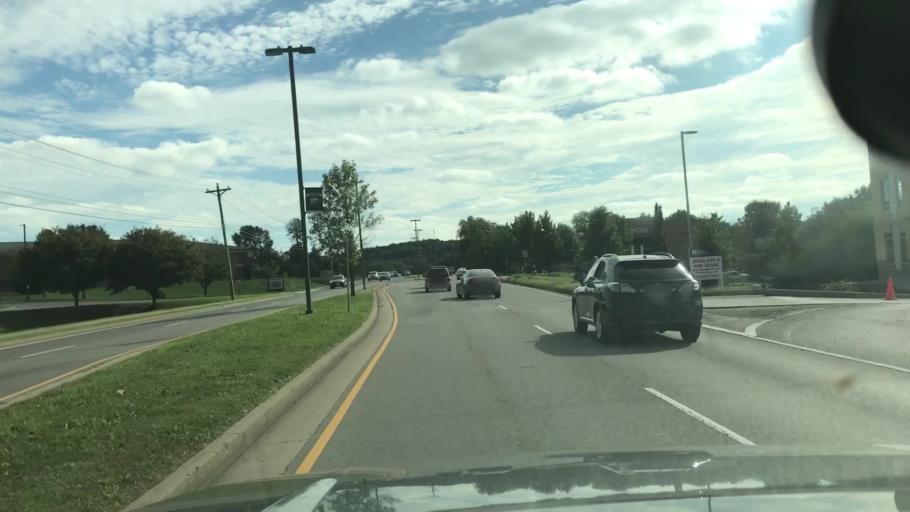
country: US
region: Tennessee
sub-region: Williamson County
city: Franklin
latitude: 35.9316
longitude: -86.8240
